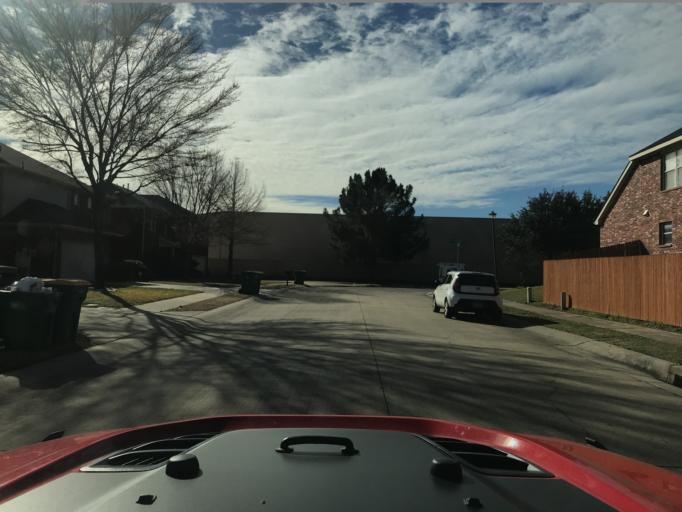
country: US
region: Texas
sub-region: Denton County
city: Lewisville
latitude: 33.0453
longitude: -97.0314
